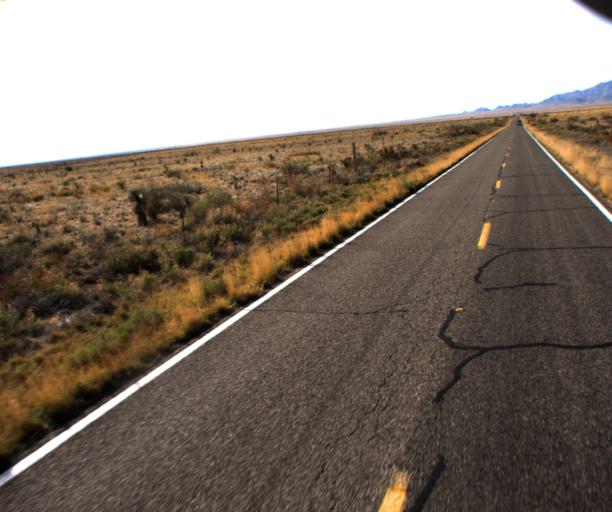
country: US
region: Arizona
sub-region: Cochise County
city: Willcox
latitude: 32.0390
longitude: -109.4800
